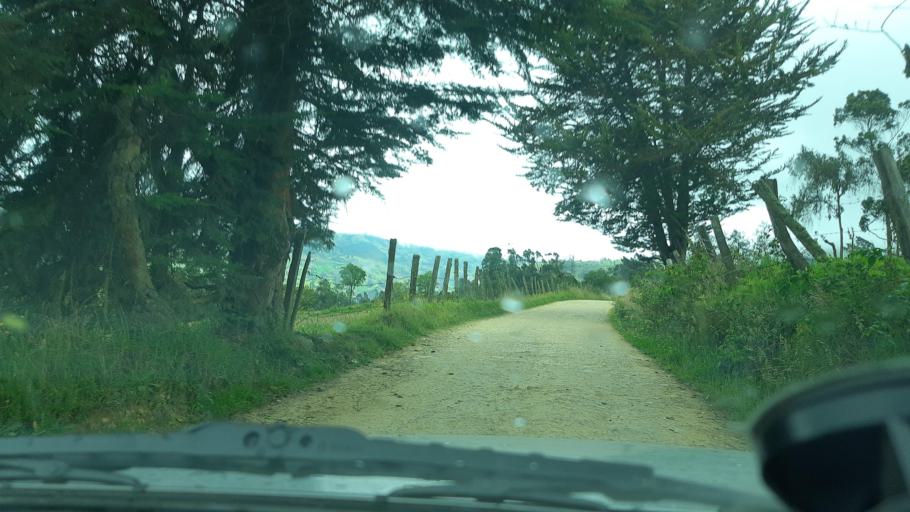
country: CO
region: Cundinamarca
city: Umbita
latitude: 5.2396
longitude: -73.4643
